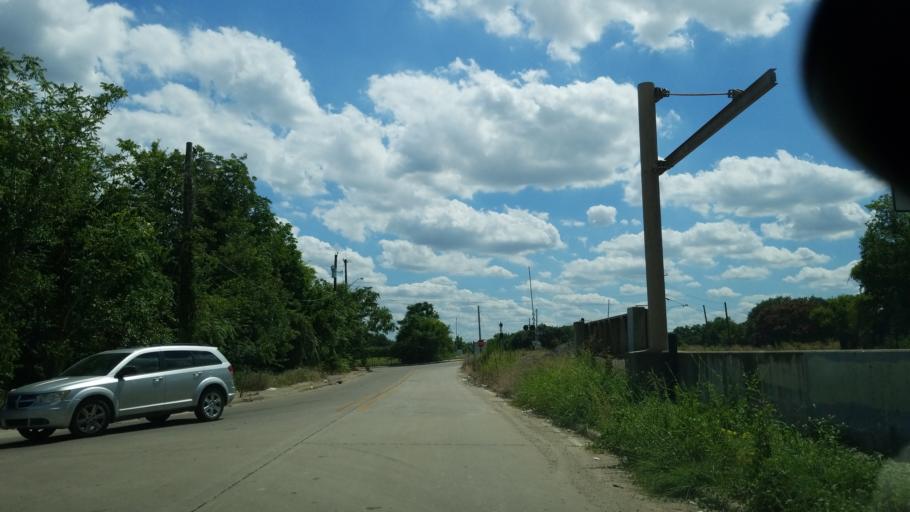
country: US
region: Texas
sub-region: Dallas County
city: Dallas
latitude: 32.7470
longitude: -96.7503
